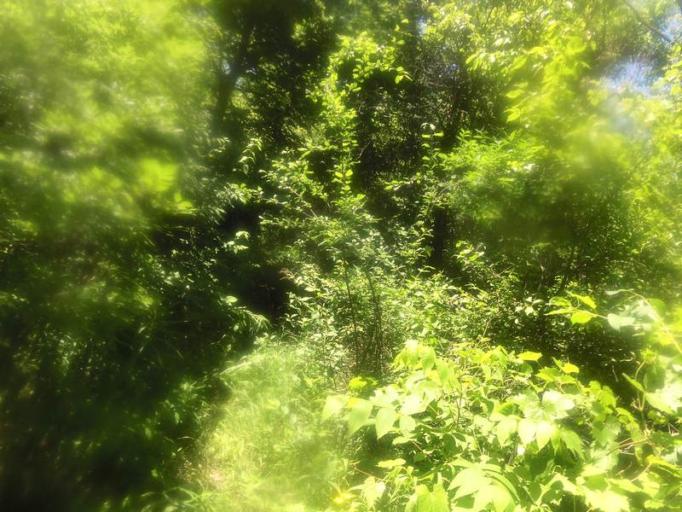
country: CA
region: Ontario
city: Kingston
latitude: 44.2439
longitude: -76.5333
